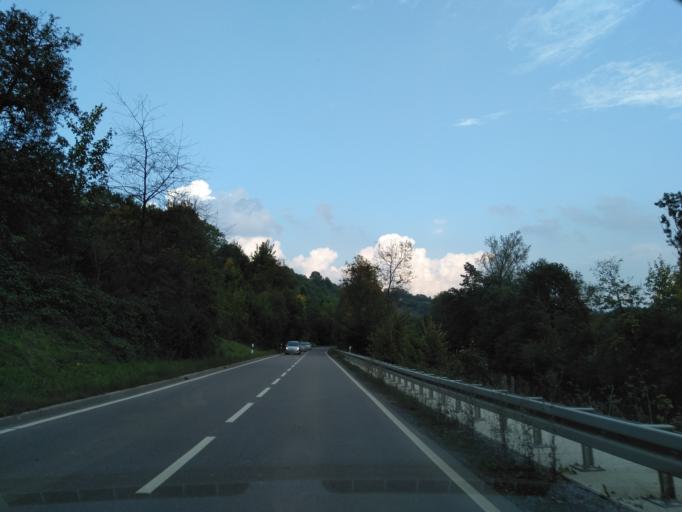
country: DE
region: Baden-Wuerttemberg
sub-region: Regierungsbezirk Stuttgart
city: Oberriexingen
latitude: 48.9414
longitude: 9.0538
